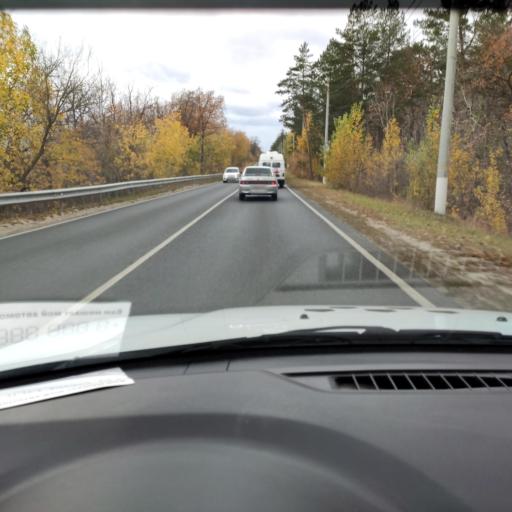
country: RU
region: Samara
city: Tol'yatti
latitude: 53.4735
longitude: 49.4035
